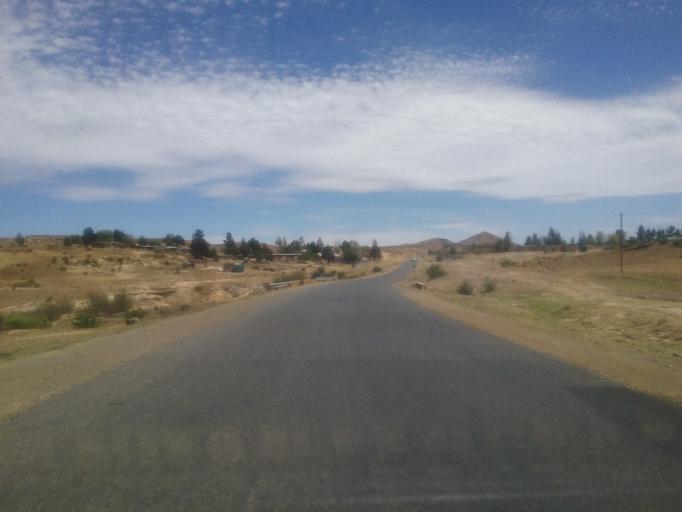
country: LS
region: Mafeteng
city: Mafeteng
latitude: -29.9453
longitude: 27.2700
